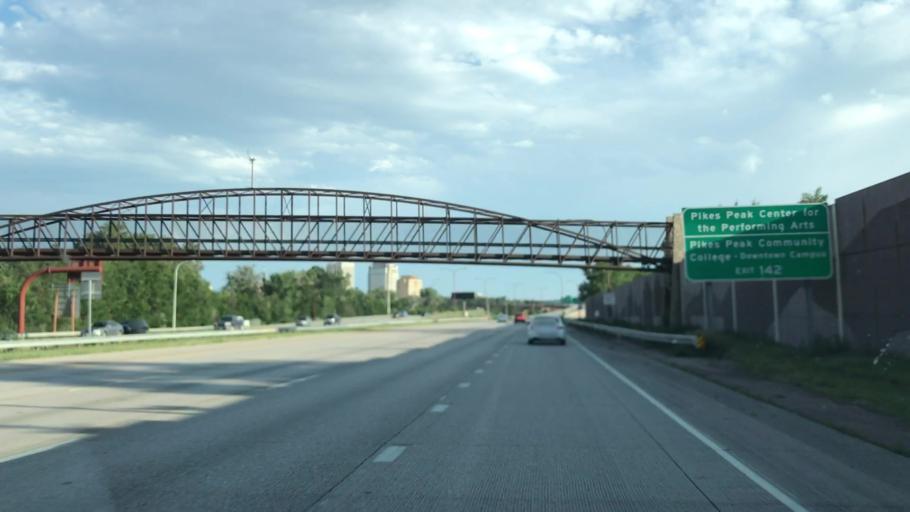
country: US
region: Colorado
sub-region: El Paso County
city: Colorado Springs
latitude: 38.8442
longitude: -104.8307
